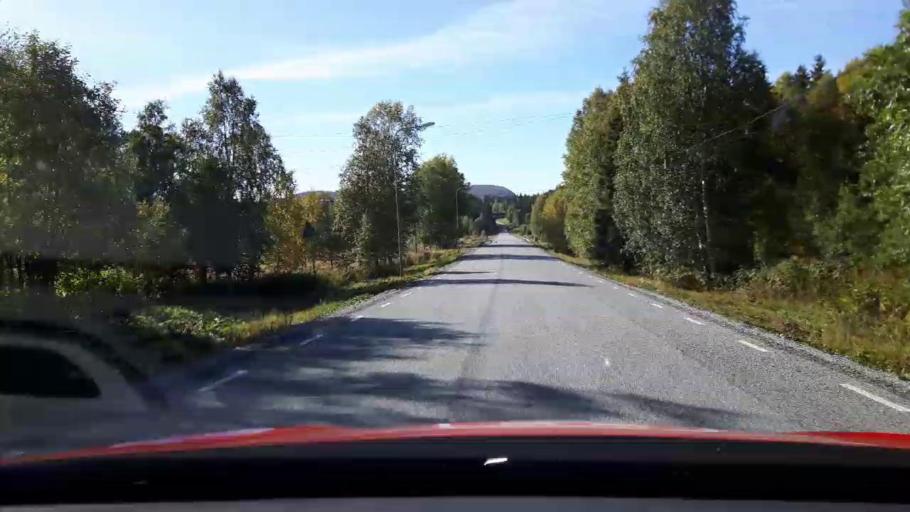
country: NO
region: Nord-Trondelag
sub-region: Royrvik
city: Royrvik
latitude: 64.7327
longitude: 14.0192
